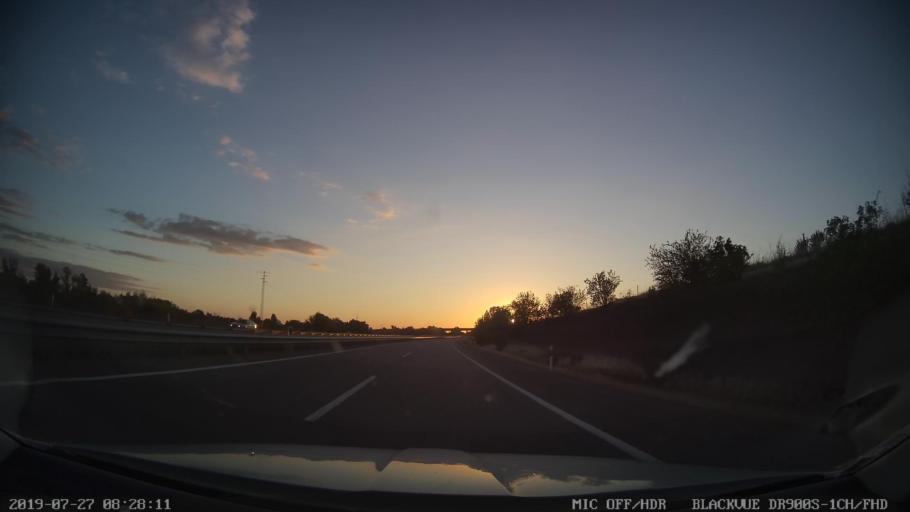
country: ES
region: Extremadura
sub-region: Provincia de Badajoz
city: Lobon
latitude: 38.8413
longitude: -6.6661
